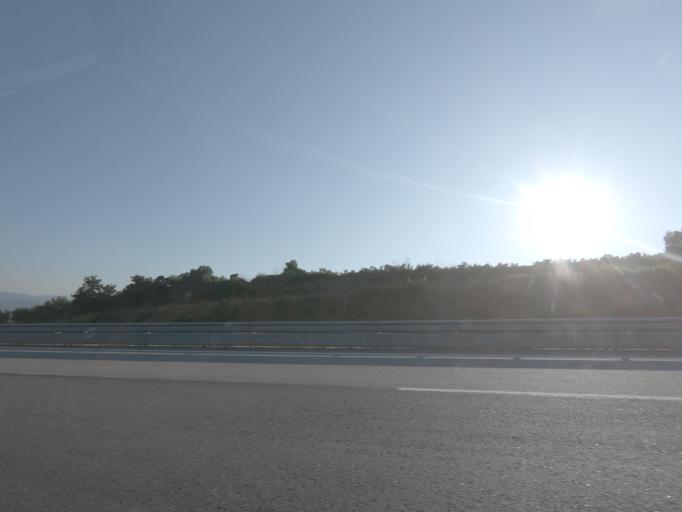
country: PT
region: Vila Real
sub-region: Peso da Regua
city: Peso da Regua
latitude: 41.1929
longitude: -7.7507
